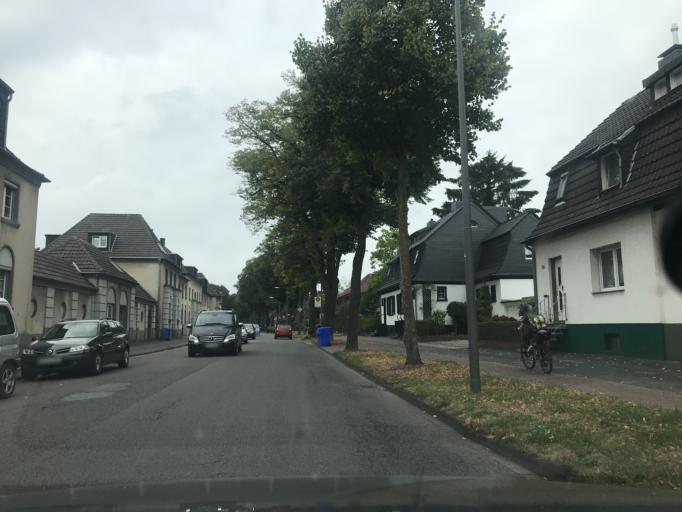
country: DE
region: North Rhine-Westphalia
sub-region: Regierungsbezirk Dusseldorf
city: Krefeld
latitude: 51.3594
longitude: 6.6314
